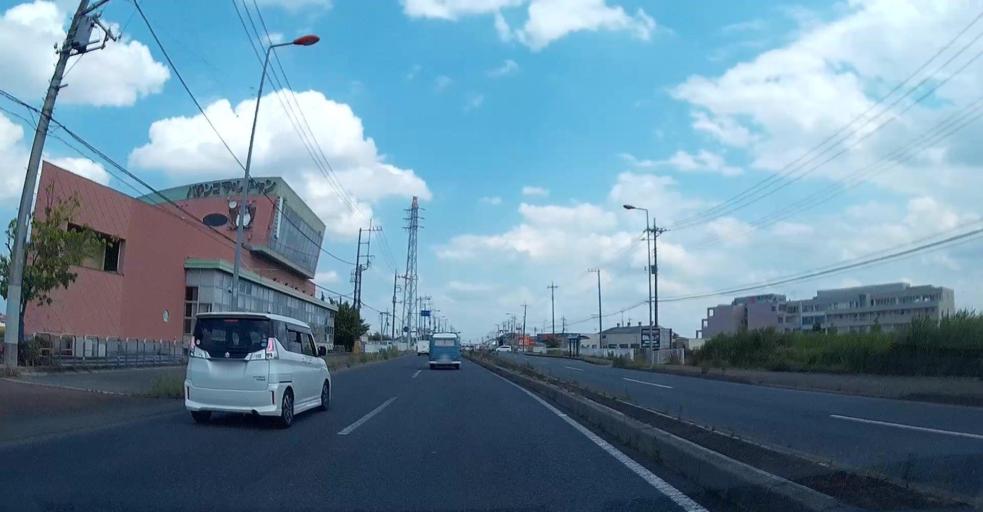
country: JP
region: Saitama
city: Kawagoe
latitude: 35.9179
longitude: 139.5170
